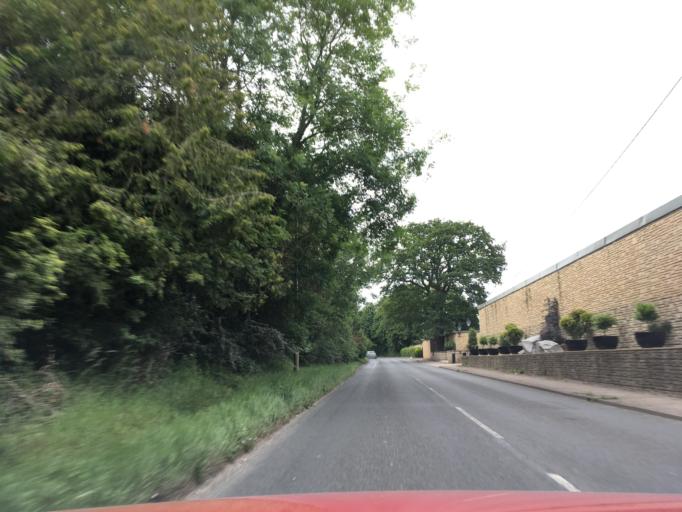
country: GB
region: England
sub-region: Oxfordshire
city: Boars Hill
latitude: 51.6994
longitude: -1.3031
